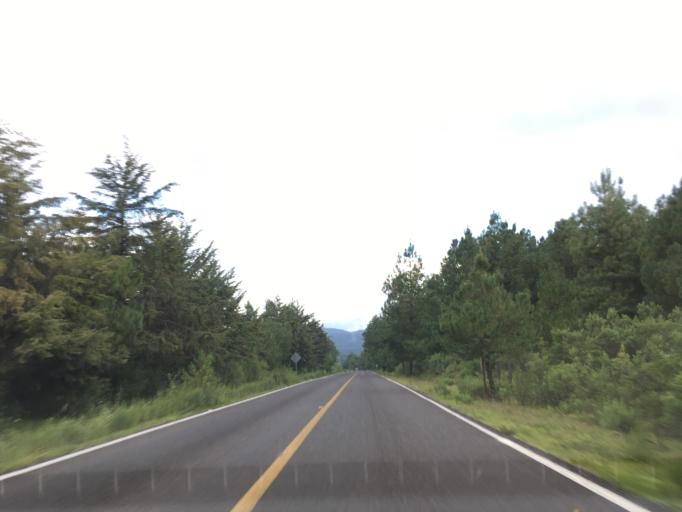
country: MX
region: Michoacan
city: Pichataro
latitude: 19.5924
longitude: -101.8327
